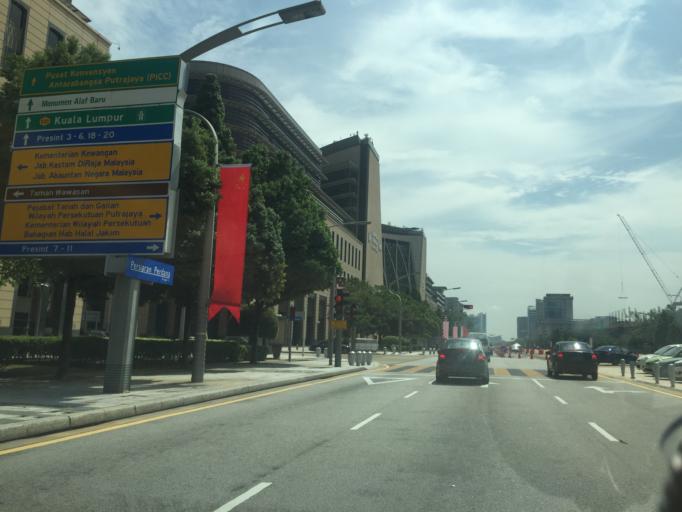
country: MY
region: Putrajaya
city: Putrajaya
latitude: 2.9286
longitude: 101.6890
